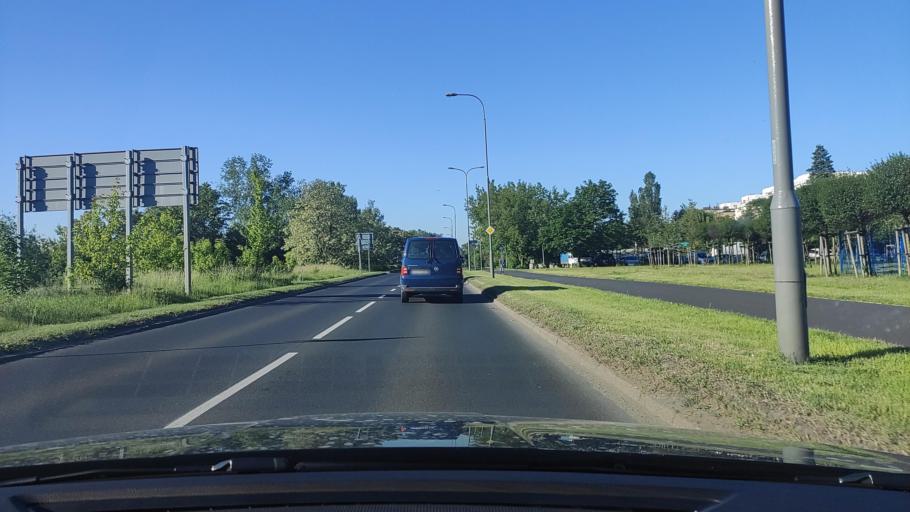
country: PL
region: Greater Poland Voivodeship
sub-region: Poznan
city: Poznan
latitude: 52.3821
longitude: 16.9213
